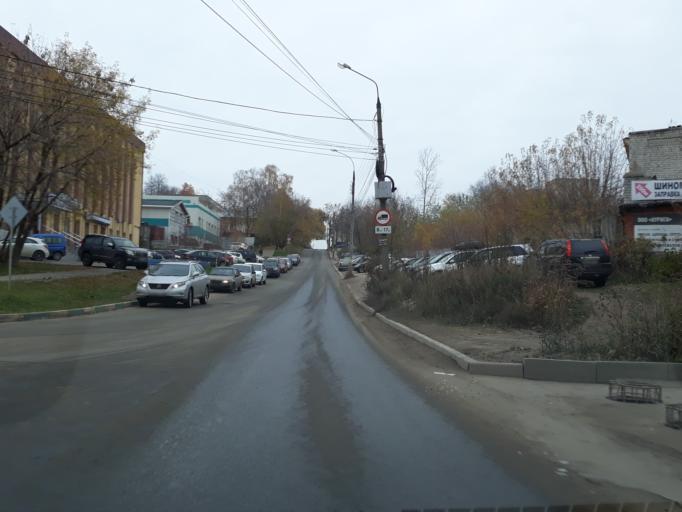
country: RU
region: Nizjnij Novgorod
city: Nizhniy Novgorod
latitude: 56.2491
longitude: 43.9836
